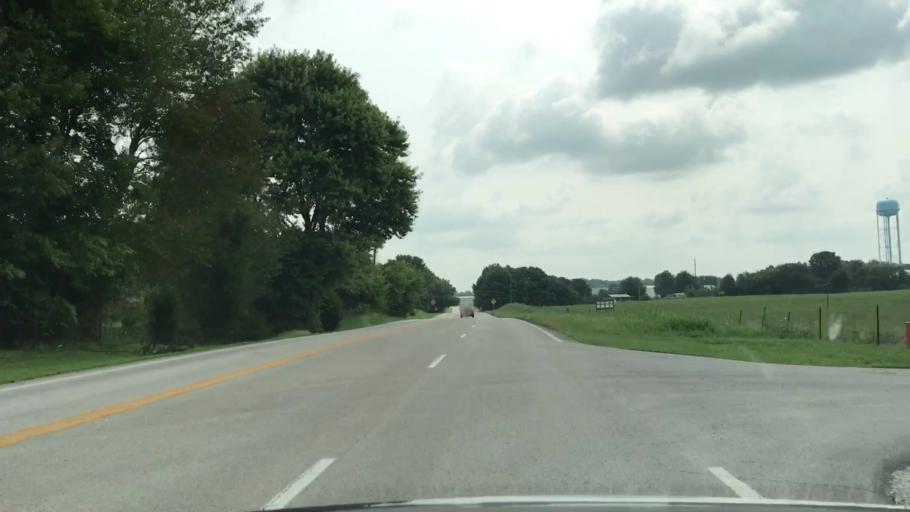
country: US
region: Kentucky
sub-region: Barren County
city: Cave City
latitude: 37.0913
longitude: -86.0827
